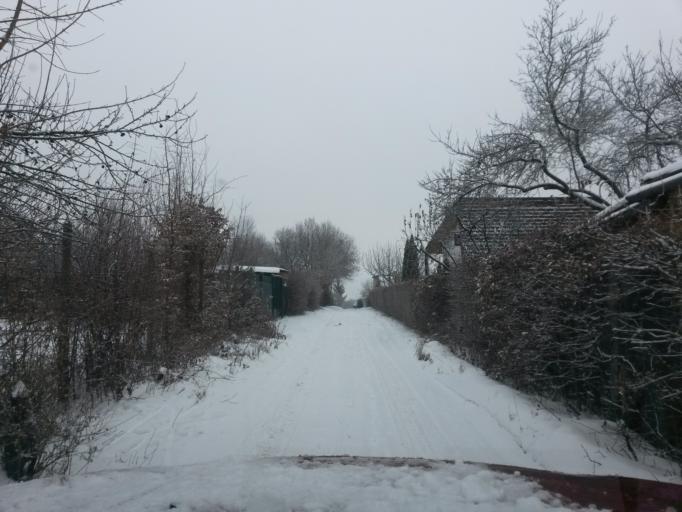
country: SK
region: Kosicky
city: Kosice
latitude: 48.7167
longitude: 21.3120
